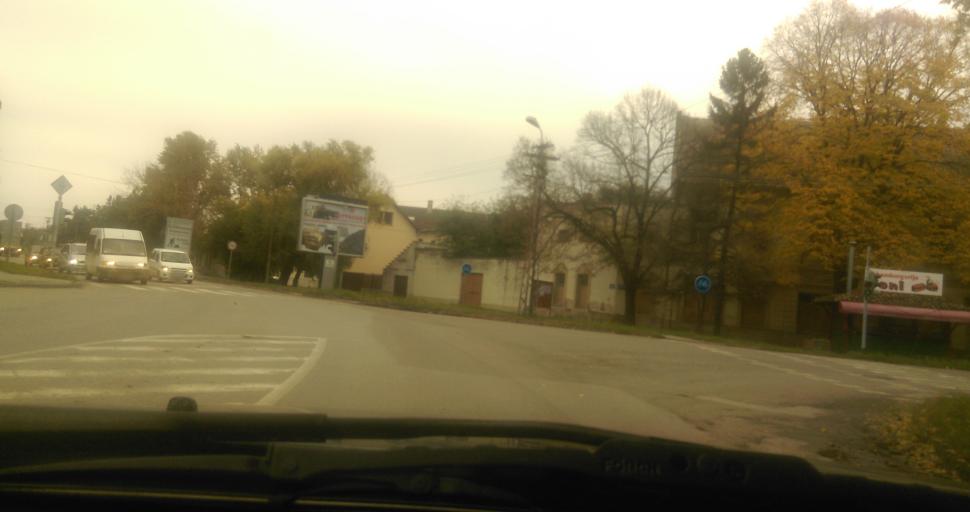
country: RS
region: Autonomna Pokrajina Vojvodina
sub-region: Juznobacki Okrug
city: Becej
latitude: 45.6219
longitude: 20.0363
